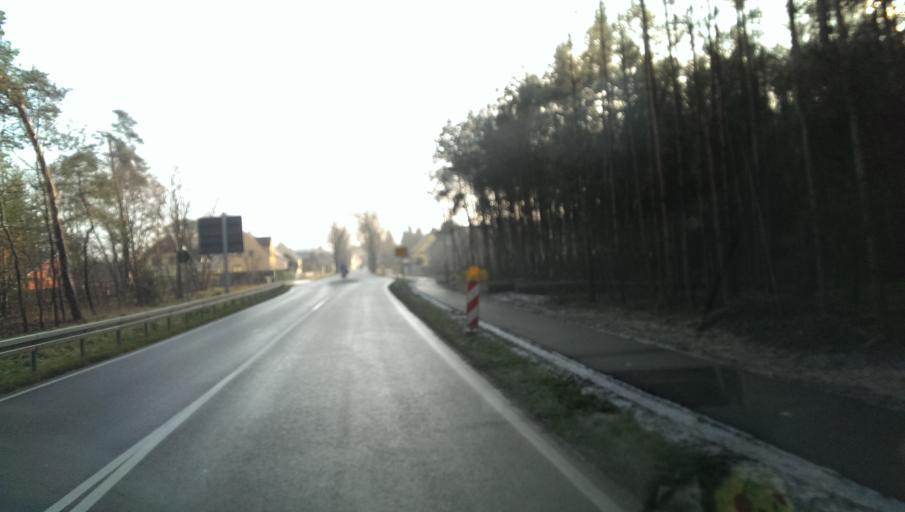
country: DE
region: Brandenburg
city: Bad Liebenwerda
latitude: 51.5514
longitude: 13.3800
